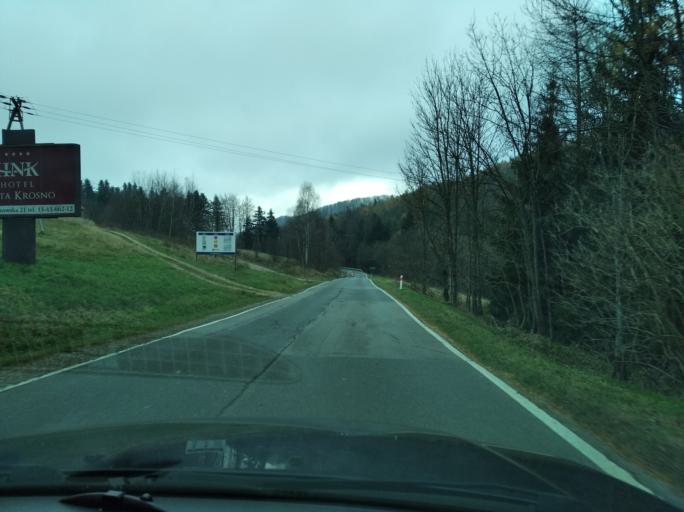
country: PL
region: Subcarpathian Voivodeship
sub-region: Powiat krosnienski
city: Korczyna
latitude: 49.7475
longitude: 21.8033
